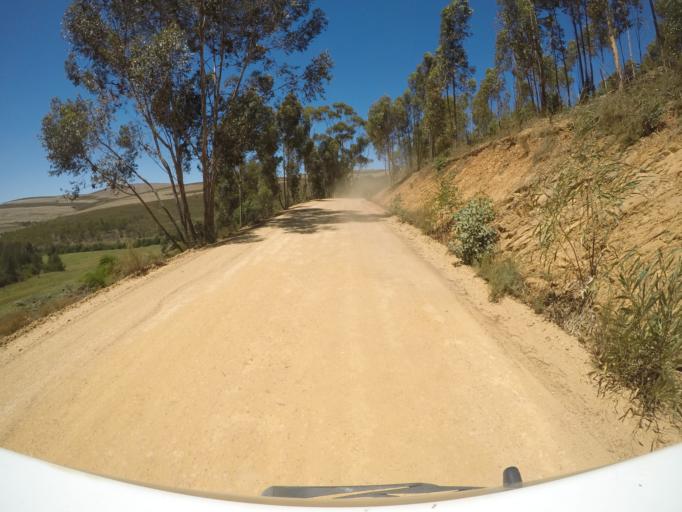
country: ZA
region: Western Cape
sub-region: Overberg District Municipality
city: Grabouw
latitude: -34.2077
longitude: 19.2133
